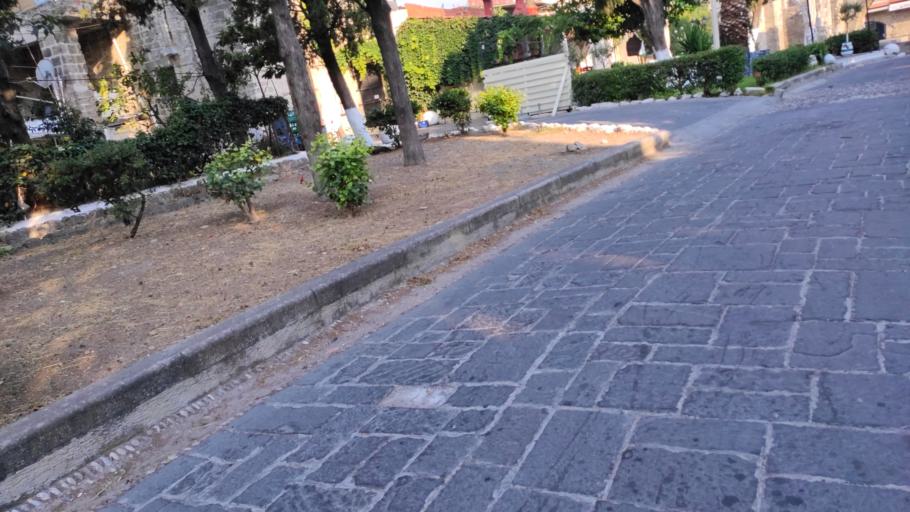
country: GR
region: South Aegean
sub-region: Nomos Dodekanisou
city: Rodos
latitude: 36.4424
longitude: 28.2312
